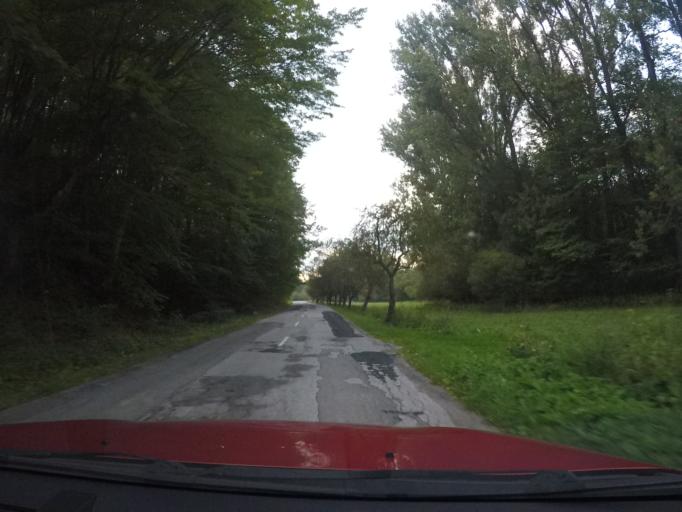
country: SK
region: Kosicky
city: Medzev
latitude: 48.6306
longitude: 20.7353
